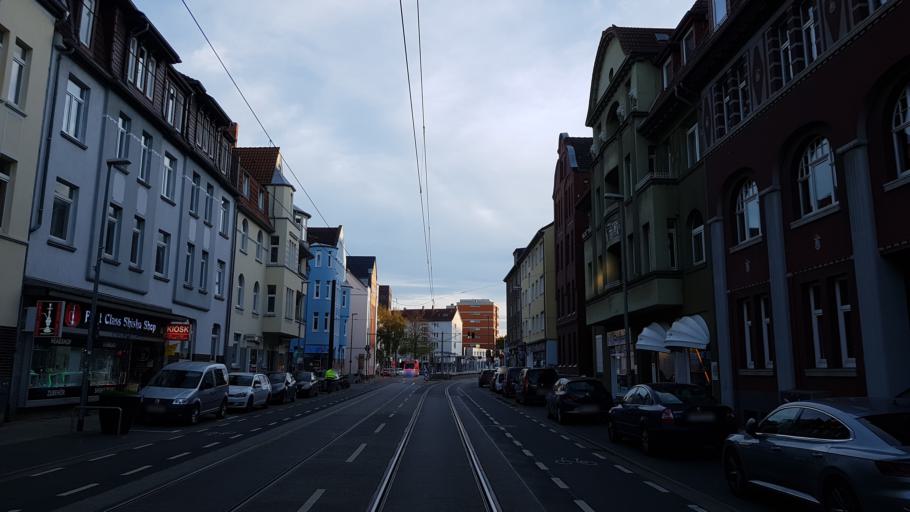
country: DE
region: Lower Saxony
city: Hannover
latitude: 52.3448
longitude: 9.7248
